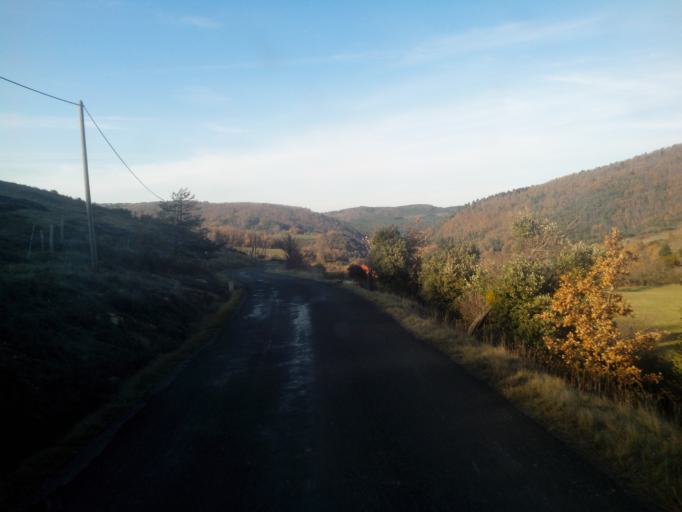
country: FR
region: Languedoc-Roussillon
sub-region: Departement de l'Aude
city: Couiza
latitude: 42.8828
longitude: 2.3211
